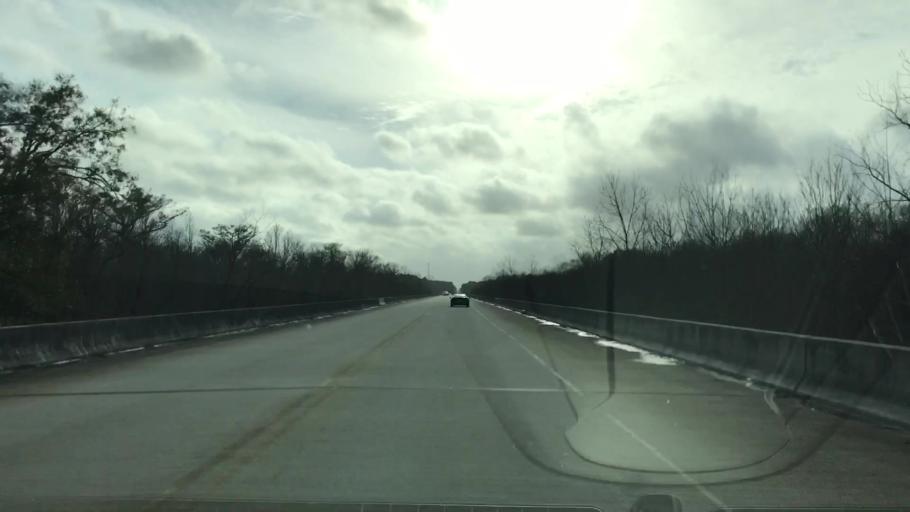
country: US
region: South Carolina
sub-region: Williamsburg County
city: Andrews
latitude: 33.3095
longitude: -79.6741
